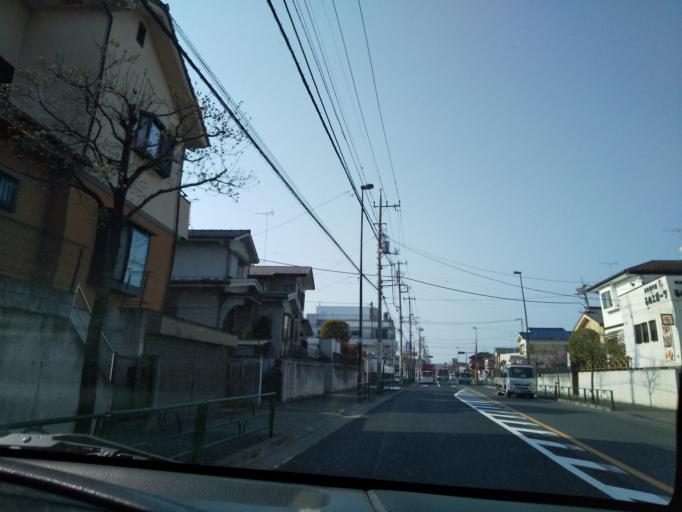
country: JP
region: Tokyo
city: Fussa
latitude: 35.7363
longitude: 139.2901
